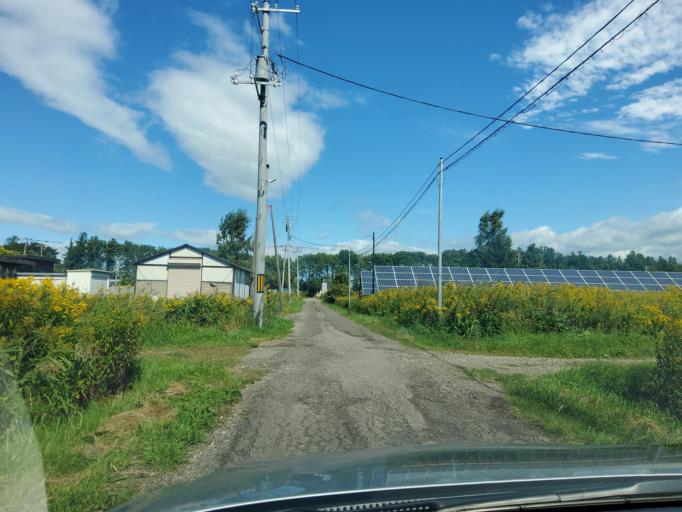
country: JP
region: Hokkaido
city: Otofuke
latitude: 42.9761
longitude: 143.2009
